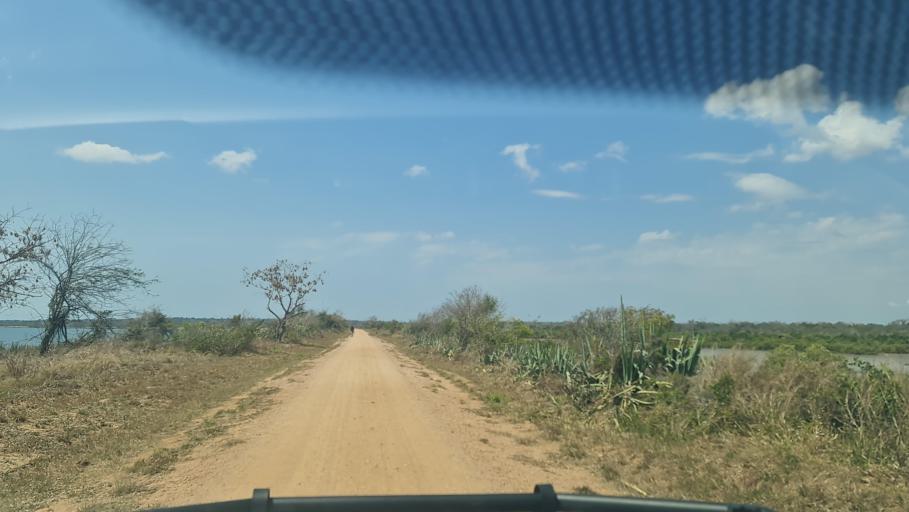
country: MZ
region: Nampula
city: Ilha de Mocambique
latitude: -15.1806
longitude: 40.5153
